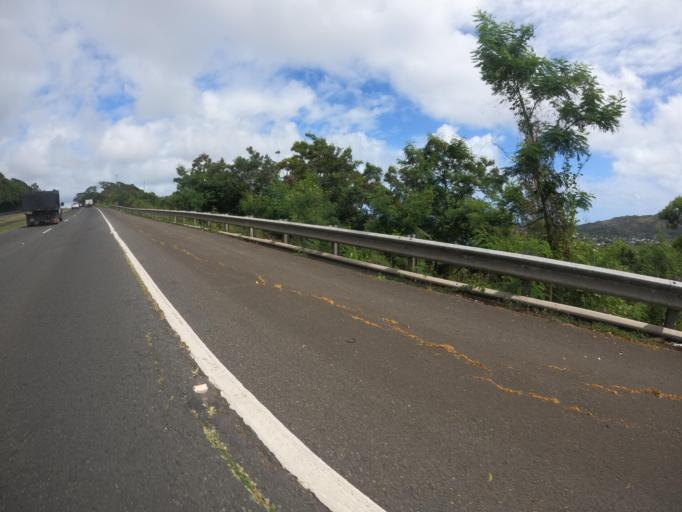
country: US
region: Hawaii
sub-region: Honolulu County
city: Maunawili
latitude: 21.3714
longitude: -157.7425
